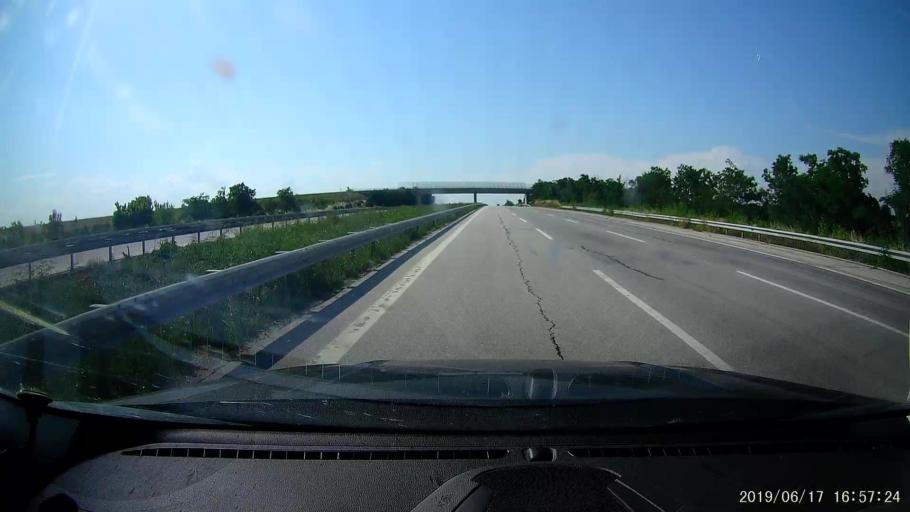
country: TR
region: Edirne
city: Haskoy
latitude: 41.5998
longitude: 26.9154
